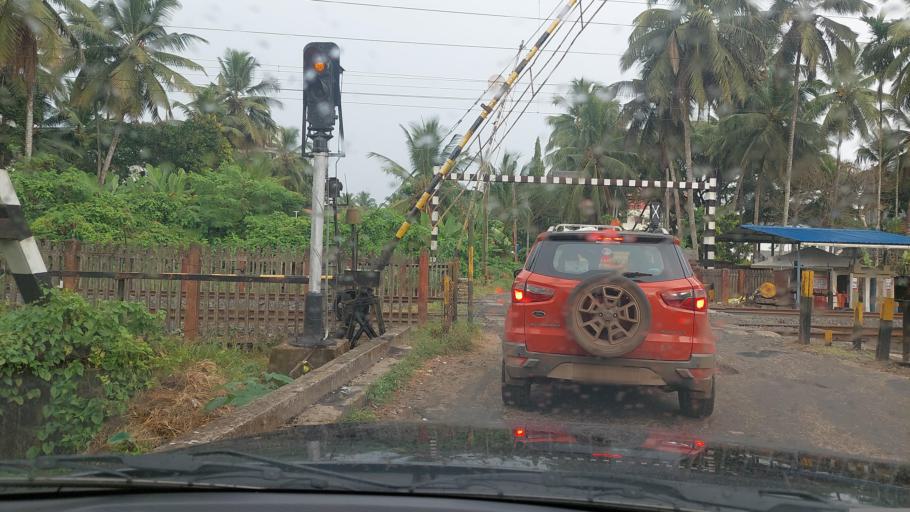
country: IN
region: Kerala
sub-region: Kozhikode
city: Kozhikode
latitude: 11.2918
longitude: 75.7625
